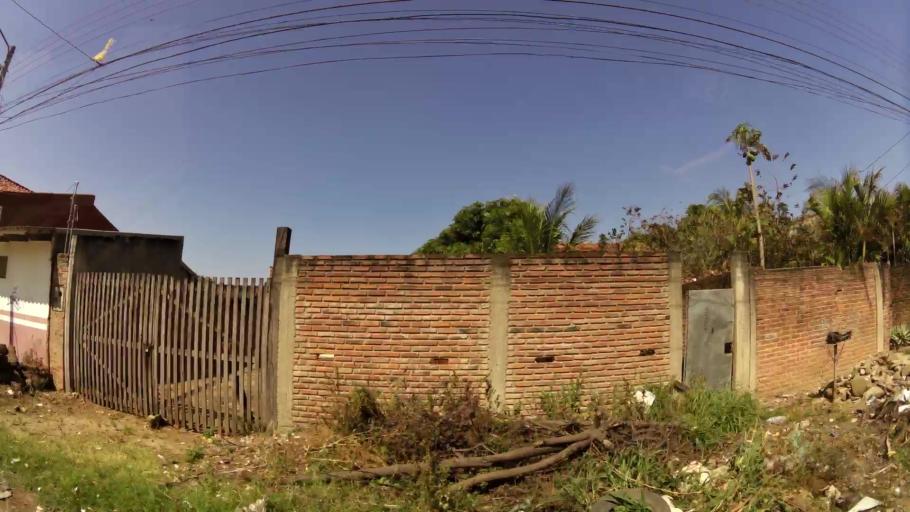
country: BO
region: Santa Cruz
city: Santa Cruz de la Sierra
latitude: -17.7447
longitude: -63.1435
